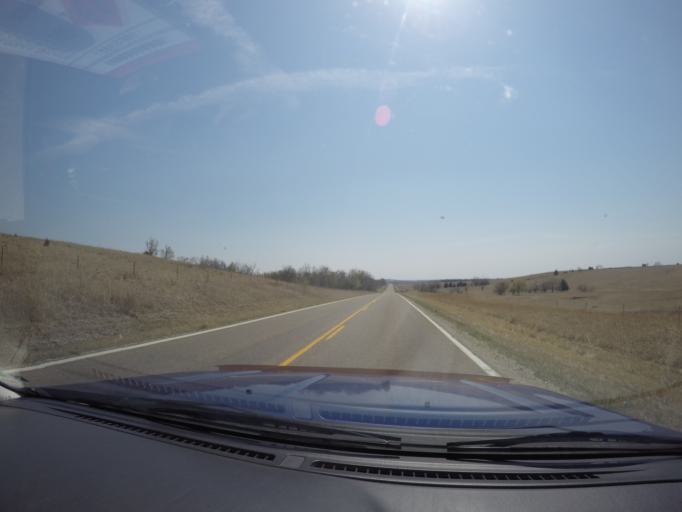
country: US
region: Kansas
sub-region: Morris County
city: Council Grove
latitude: 38.7491
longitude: -96.5012
